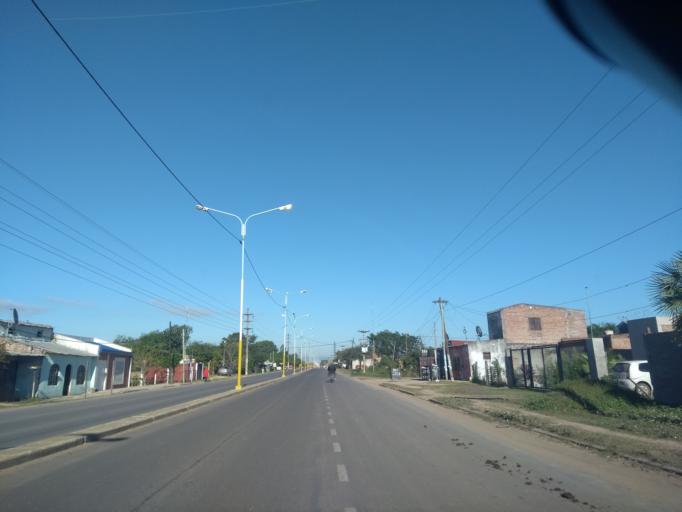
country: AR
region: Chaco
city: Barranqueras
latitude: -27.4664
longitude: -58.9179
